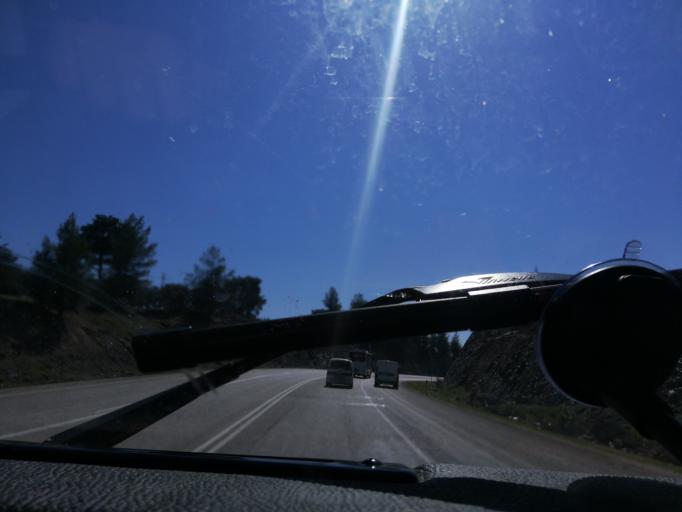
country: TR
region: Mugla
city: Kemer
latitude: 36.6101
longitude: 29.3585
